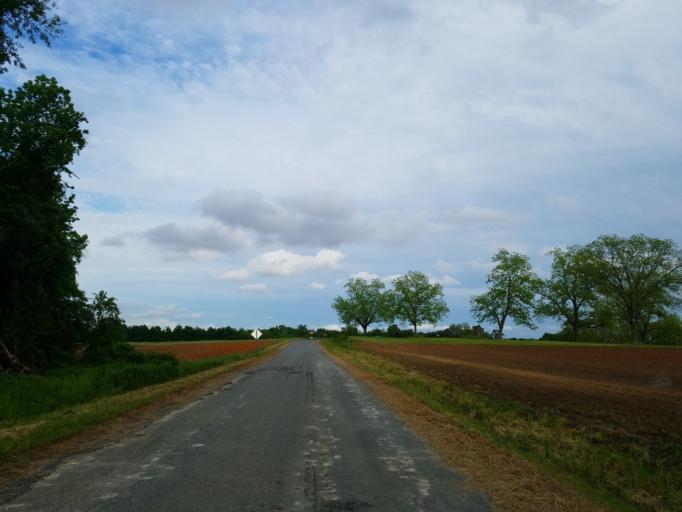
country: US
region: Georgia
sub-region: Dooly County
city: Unadilla
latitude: 32.1869
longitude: -83.7574
